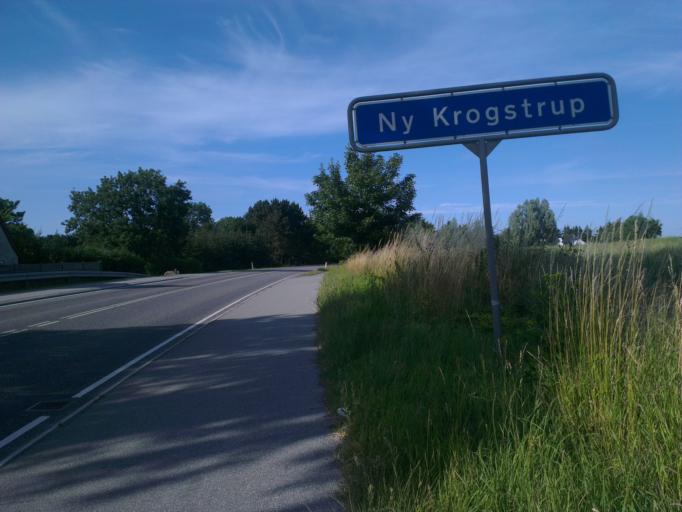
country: DK
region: Capital Region
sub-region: Frederikssund Kommune
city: Skibby
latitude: 55.7738
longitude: 11.9603
